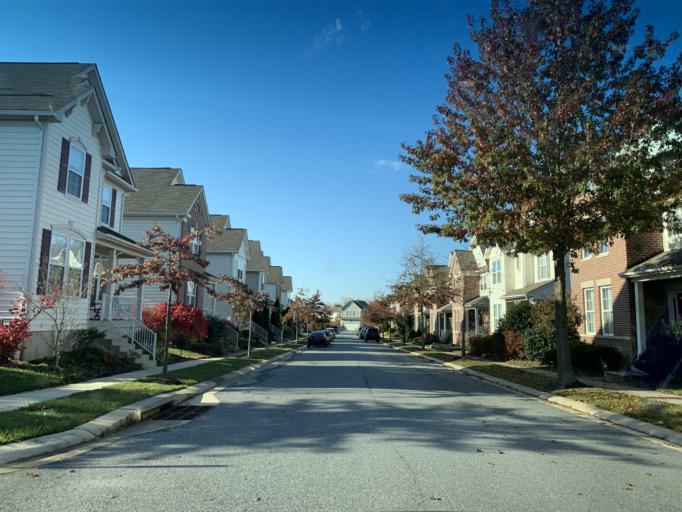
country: US
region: Maryland
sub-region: Baltimore County
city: Middle River
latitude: 39.3427
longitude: -76.4458
